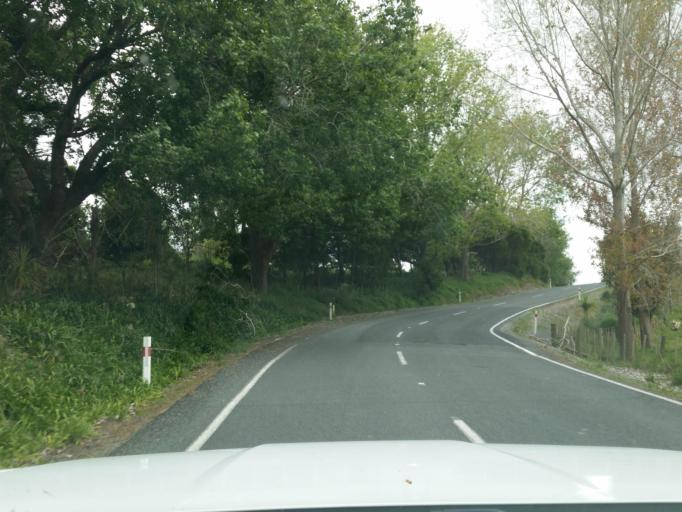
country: NZ
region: Auckland
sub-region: Auckland
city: Wellsford
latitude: -36.2281
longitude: 174.3718
